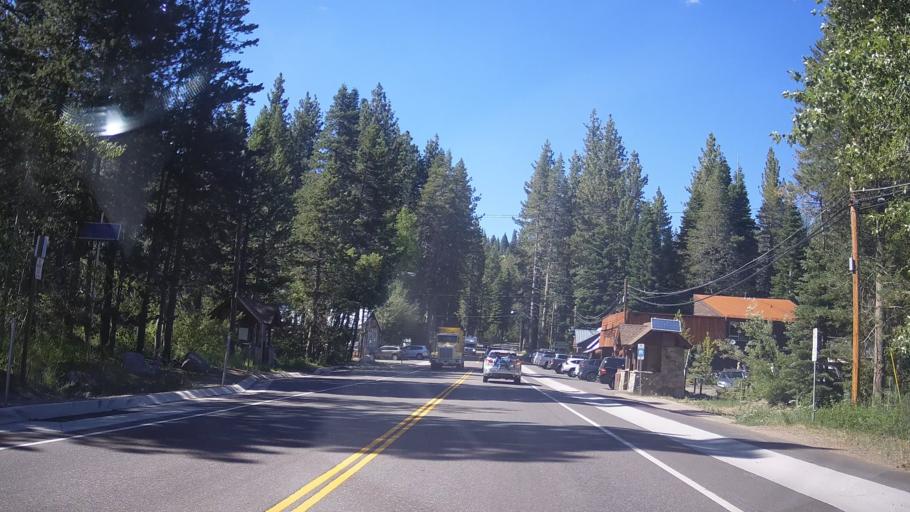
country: US
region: California
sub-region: Placer County
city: Sunnyside-Tahoe City
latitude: 39.1397
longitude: -120.1543
